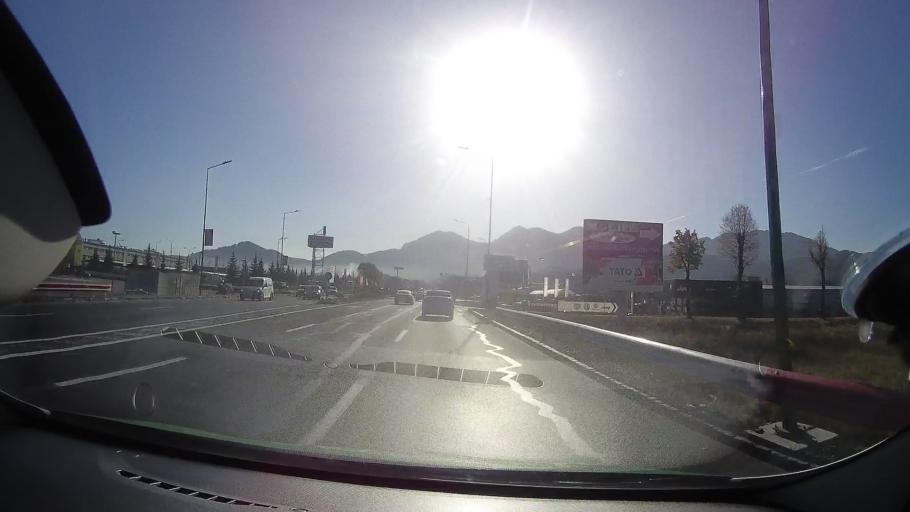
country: RO
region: Brasov
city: Brasov
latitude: 45.6264
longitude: 25.6424
